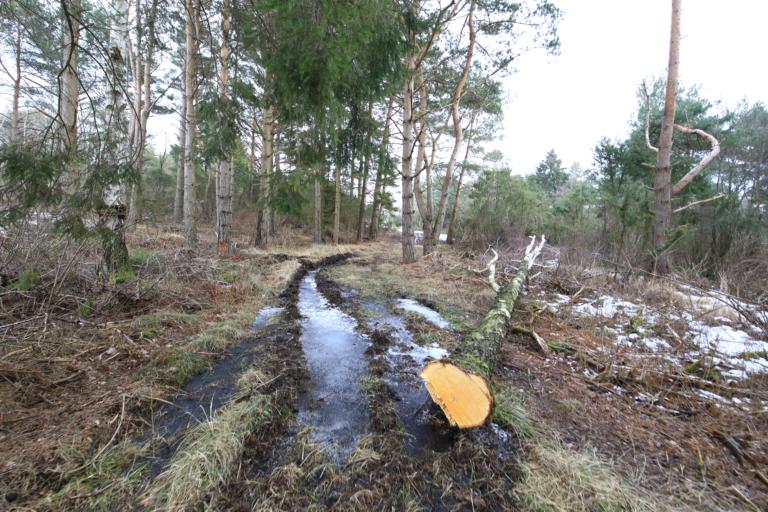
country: SE
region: Halland
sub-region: Kungsbacka Kommun
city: Frillesas
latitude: 57.2194
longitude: 12.1406
